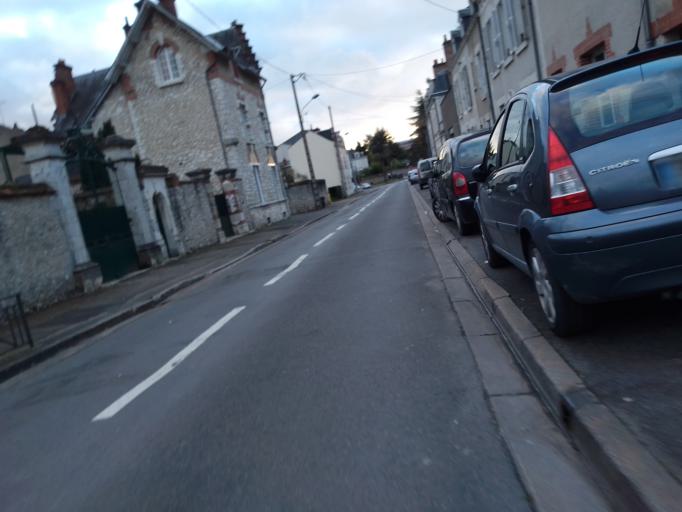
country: FR
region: Centre
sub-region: Departement du Loir-et-Cher
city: Blois
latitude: 47.5922
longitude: 1.3414
